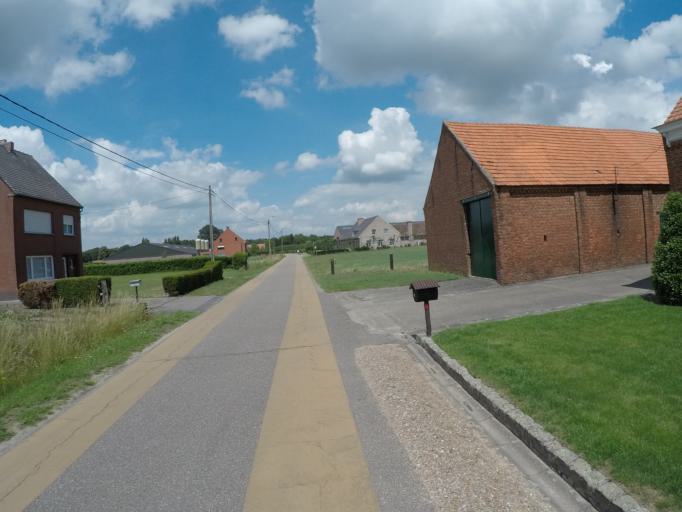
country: BE
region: Flanders
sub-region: Provincie Antwerpen
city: Beerse
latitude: 51.2762
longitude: 4.8502
